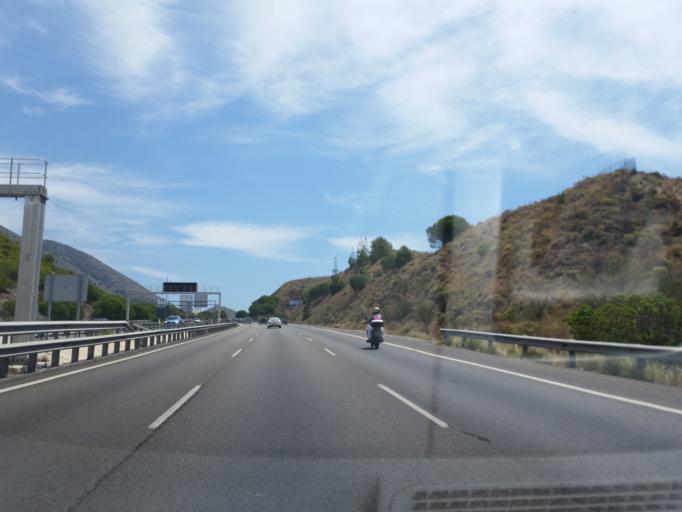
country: ES
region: Andalusia
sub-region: Provincia de Malaga
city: Mijas
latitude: 36.5764
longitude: -4.6153
